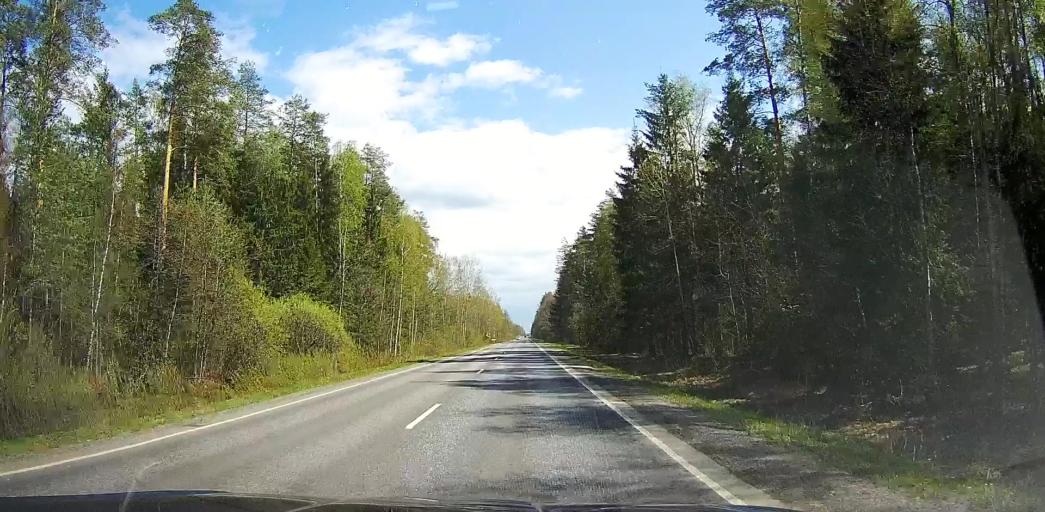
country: RU
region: Moskovskaya
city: Davydovo
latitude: 55.5514
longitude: 38.7596
